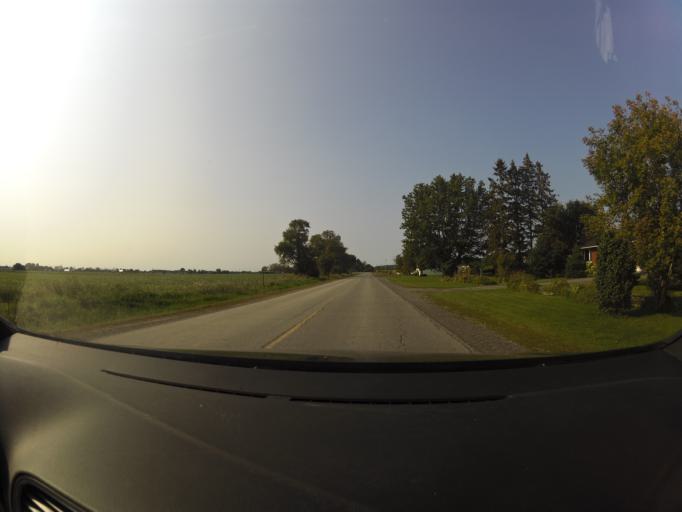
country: CA
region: Ontario
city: Carleton Place
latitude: 45.3431
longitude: -76.0575
